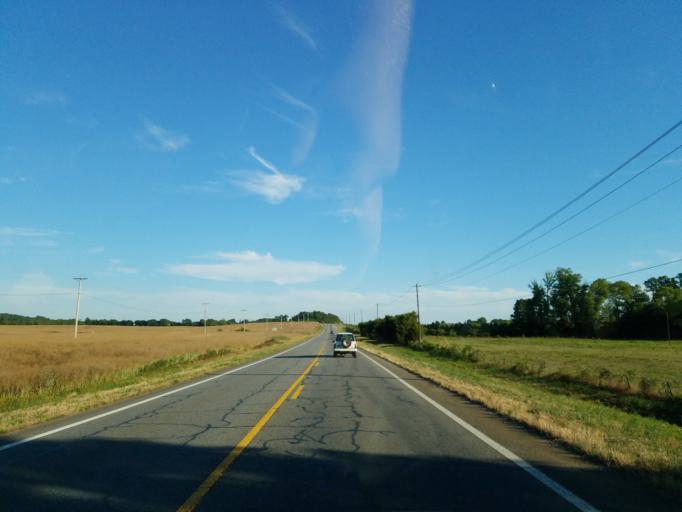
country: US
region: Georgia
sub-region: Bartow County
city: Adairsville
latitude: 34.4083
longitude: -84.9361
